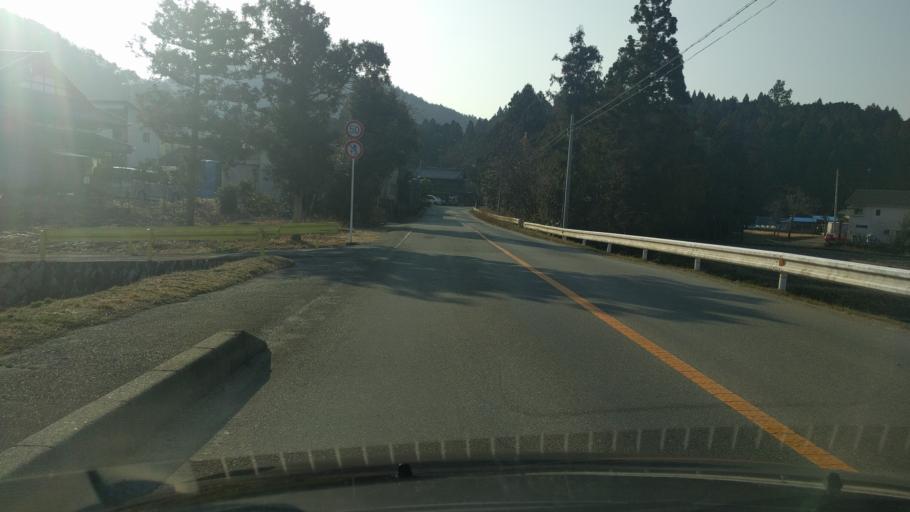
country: JP
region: Fukushima
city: Iwaki
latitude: 37.0667
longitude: 140.8049
